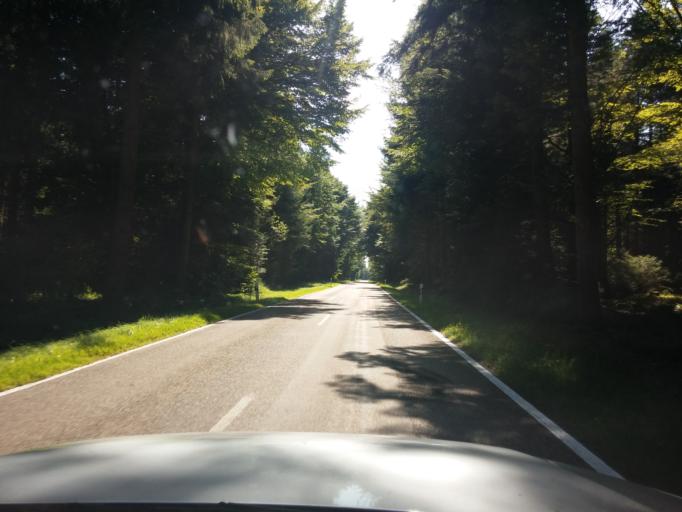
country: DE
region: Baden-Wuerttemberg
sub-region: Tuebingen Region
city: Leutkirch im Allgau
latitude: 47.8442
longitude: 10.0395
